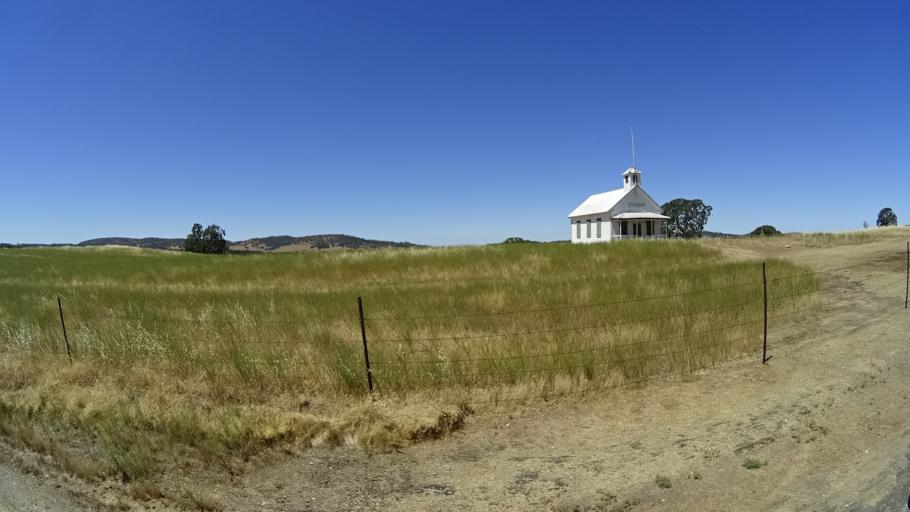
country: US
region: California
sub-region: Calaveras County
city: Copperopolis
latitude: 38.0404
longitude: -120.7288
